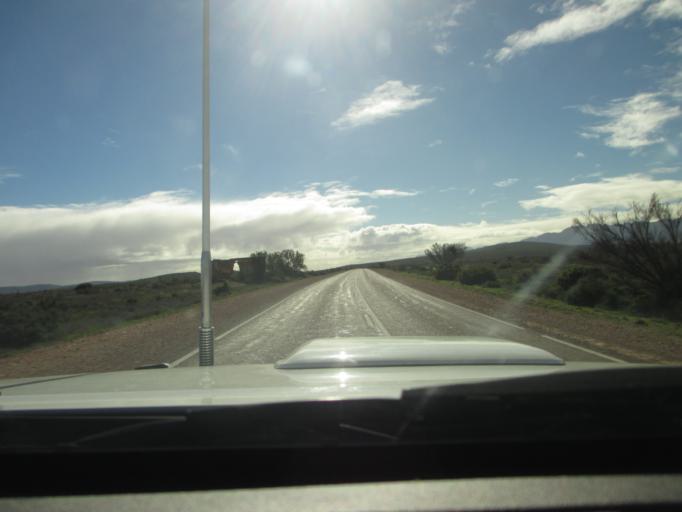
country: AU
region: South Australia
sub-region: Flinders Ranges
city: Quorn
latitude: -31.7581
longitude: 138.3321
